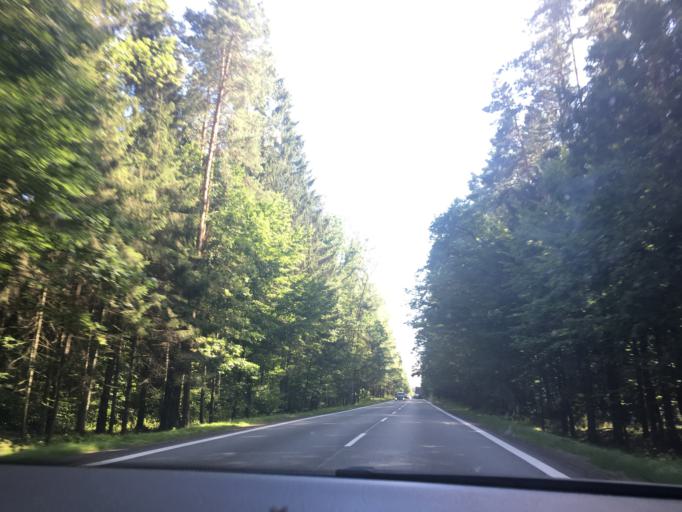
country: PL
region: Podlasie
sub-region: Powiat bialostocki
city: Wasilkow
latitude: 53.2896
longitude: 23.1228
